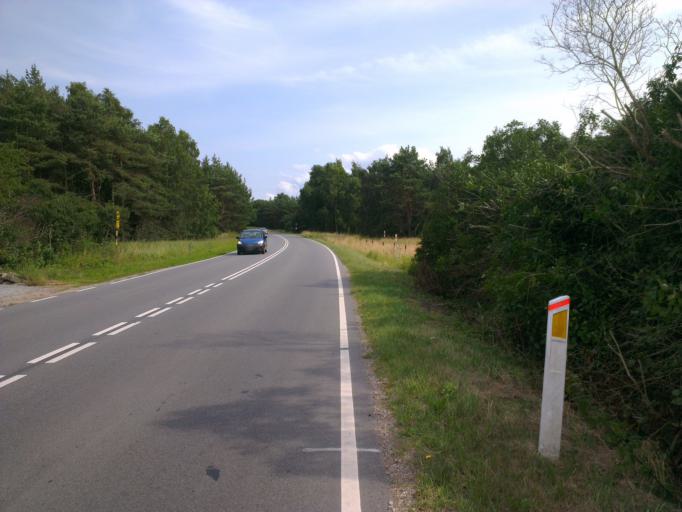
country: DK
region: Capital Region
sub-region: Frederikssund Kommune
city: Jaegerspris
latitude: 55.8982
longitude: 11.9468
